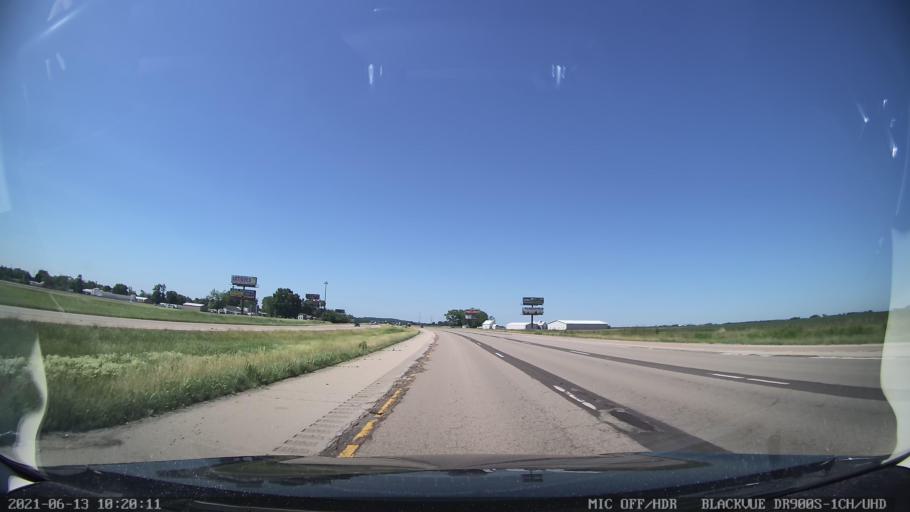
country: US
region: Illinois
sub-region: Logan County
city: Lincoln
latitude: 40.0731
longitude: -89.4442
